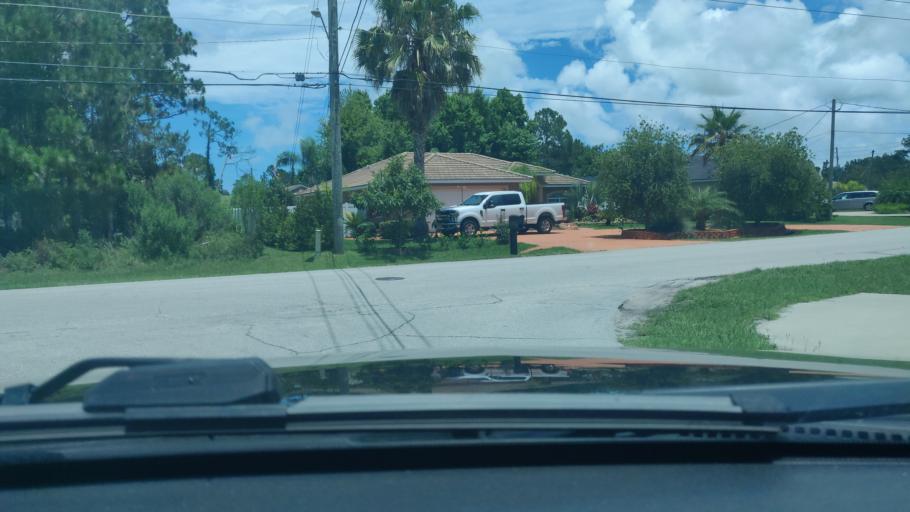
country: US
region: Florida
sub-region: Flagler County
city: Bunnell
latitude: 29.5179
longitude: -81.2563
